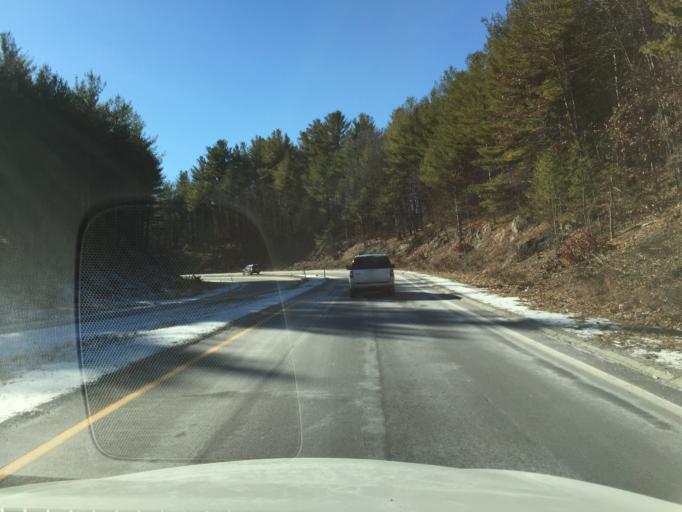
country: US
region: Massachusetts
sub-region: Norfolk County
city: Foxborough
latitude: 42.0447
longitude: -71.2452
